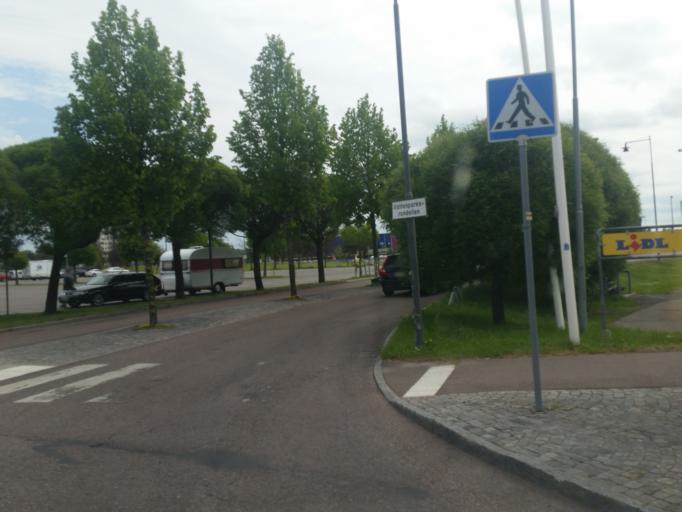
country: SE
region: Dalarna
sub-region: Borlange Kommun
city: Borlaenge
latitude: 60.4825
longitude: 15.4144
